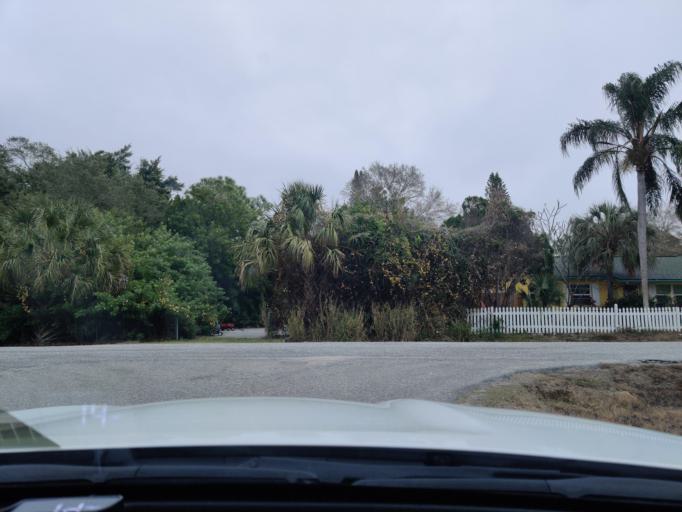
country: US
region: Florida
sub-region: Sarasota County
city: South Venice
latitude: 27.0387
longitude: -82.4024
